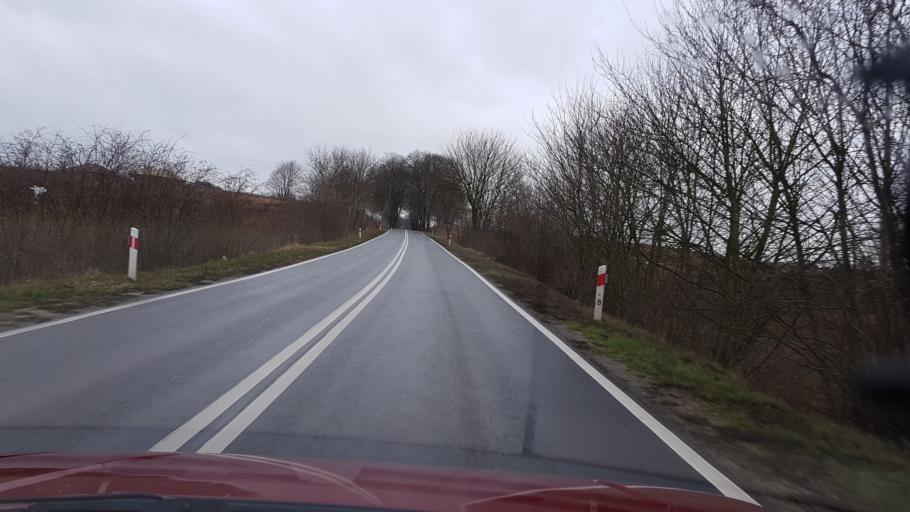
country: PL
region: West Pomeranian Voivodeship
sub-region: Powiat gryfinski
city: Gryfino
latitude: 53.2581
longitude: 14.5128
